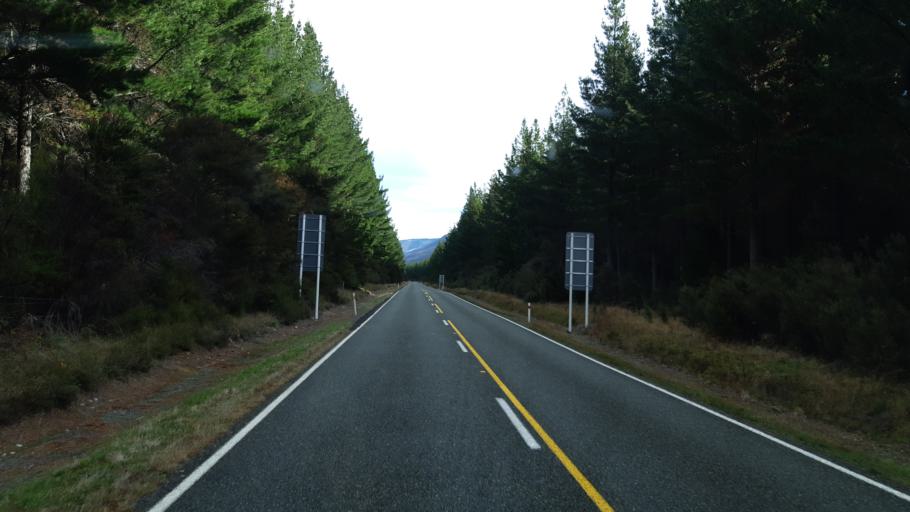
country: NZ
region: Tasman
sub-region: Tasman District
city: Wakefield
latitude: -41.7173
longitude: 173.0757
